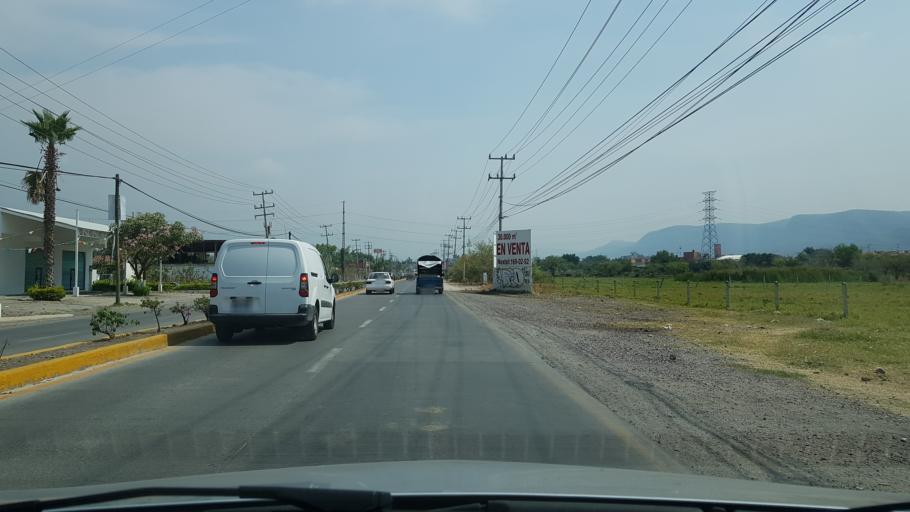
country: MX
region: Morelos
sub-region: Xochitepec
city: Chiconcuac
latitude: 18.8074
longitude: -99.1951
